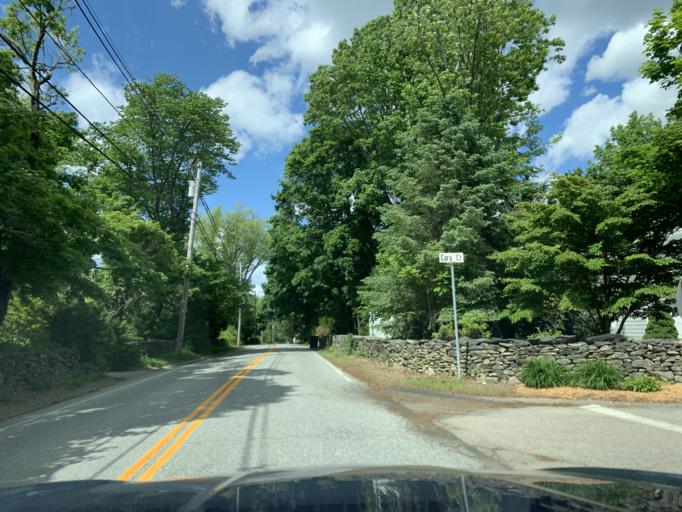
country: US
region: Rhode Island
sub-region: Kent County
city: East Greenwich
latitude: 41.6331
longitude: -71.4589
